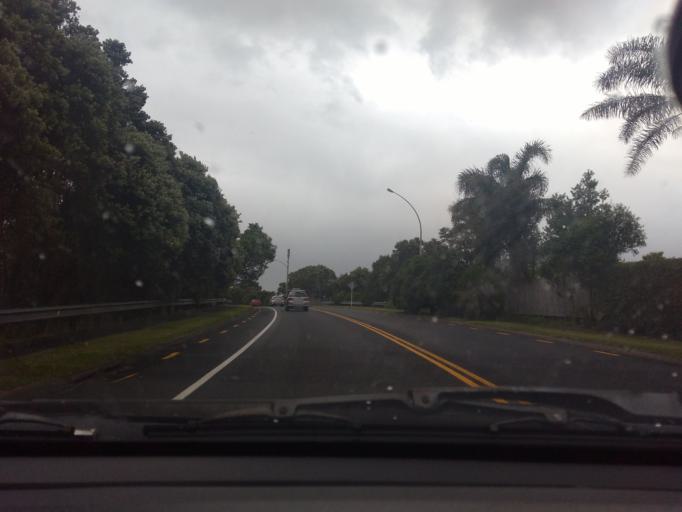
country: NZ
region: Auckland
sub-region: Auckland
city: Auckland
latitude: -36.8757
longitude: 174.7258
